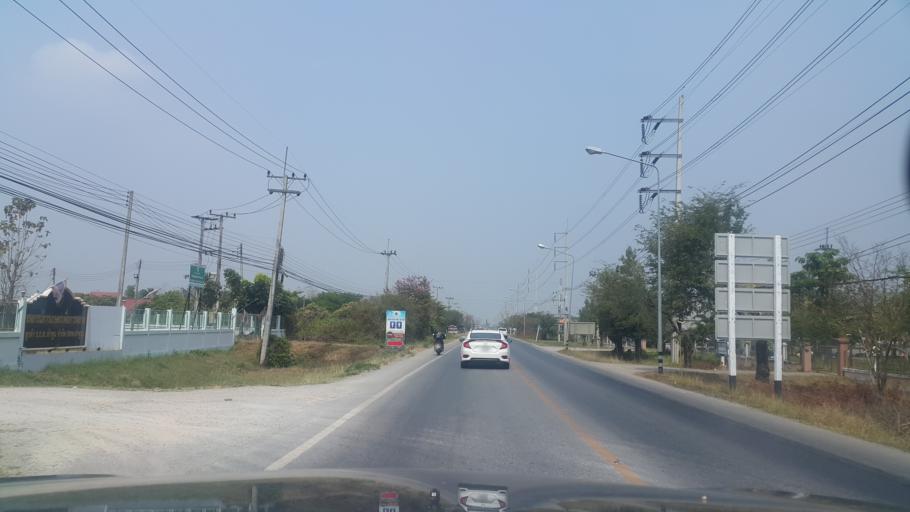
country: TH
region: Lamphun
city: Pa Sang
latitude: 18.4745
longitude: 98.9501
